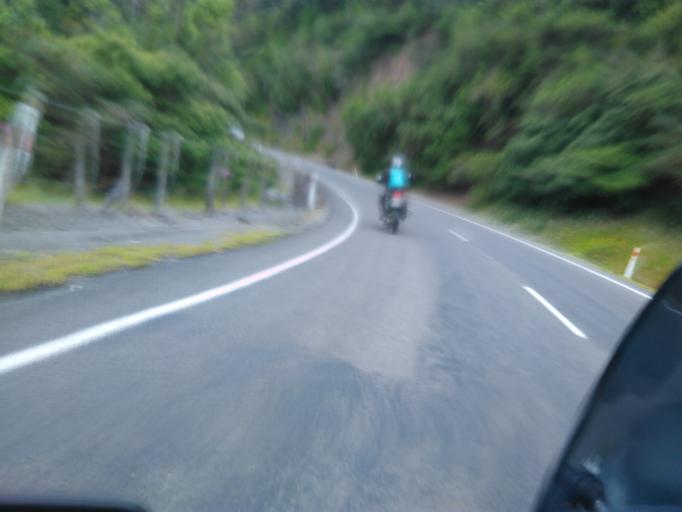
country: NZ
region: Bay of Plenty
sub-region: Opotiki District
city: Opotiki
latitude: -38.3597
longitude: 177.4529
